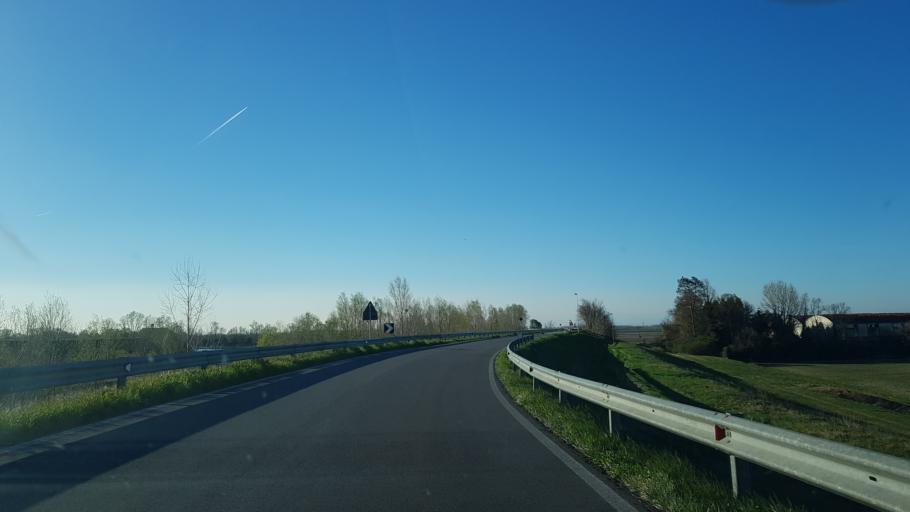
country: IT
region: Veneto
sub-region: Provincia di Rovigo
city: Lendinara
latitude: 45.1153
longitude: 11.6038
